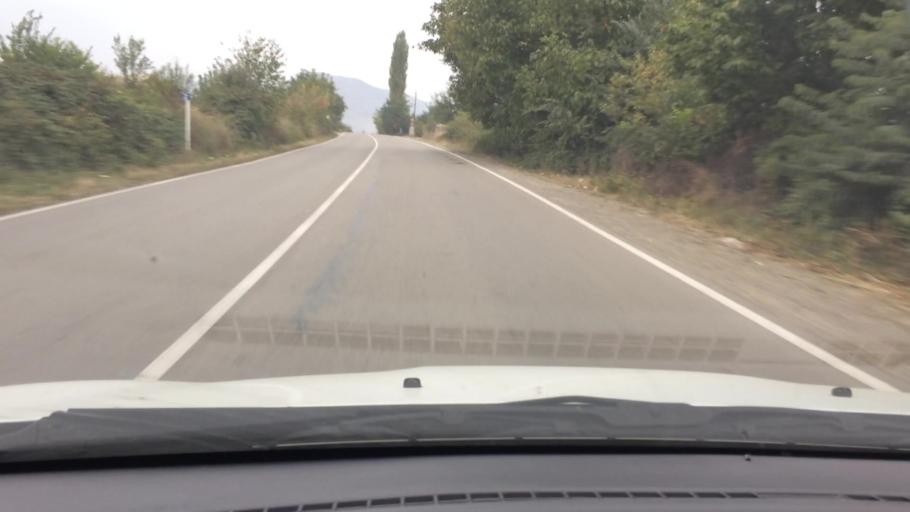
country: AM
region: Tavush
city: Bagratashen
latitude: 41.2353
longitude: 44.8090
